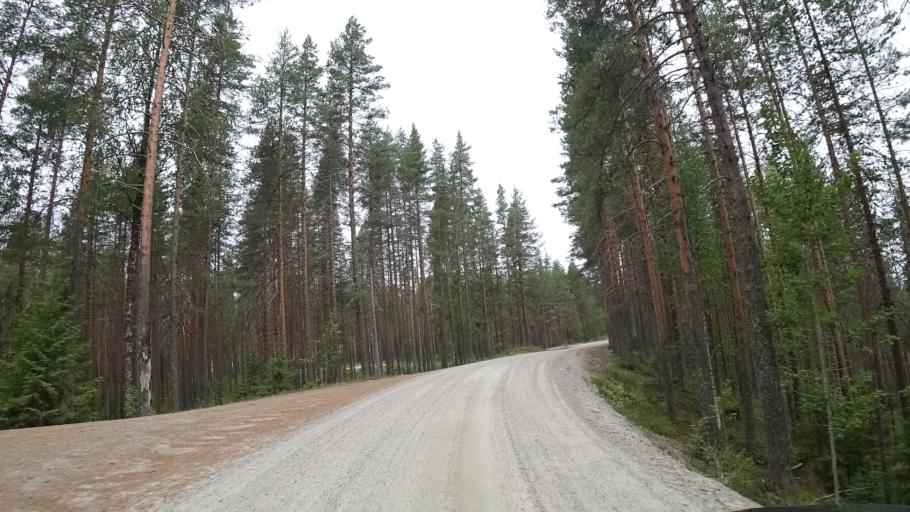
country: FI
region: North Karelia
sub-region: Pielisen Karjala
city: Lieksa
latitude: 63.2082
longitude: 30.4207
